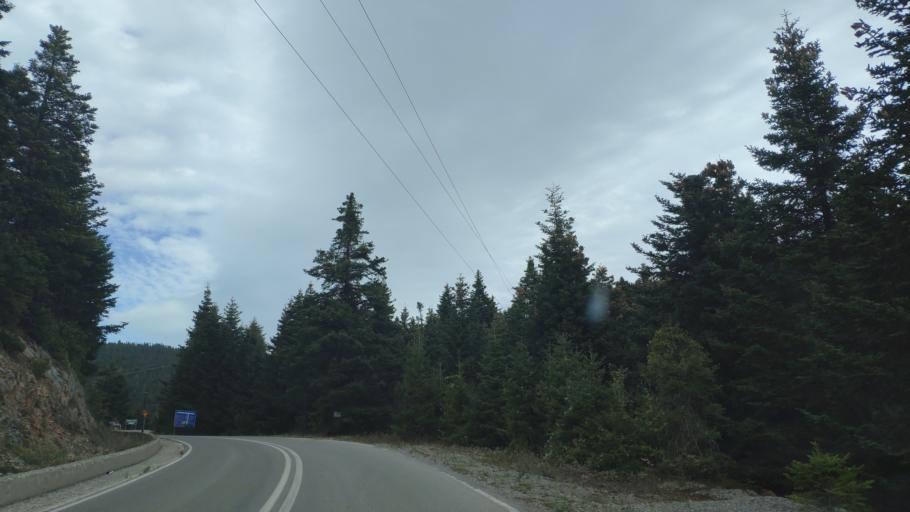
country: GR
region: Central Greece
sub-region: Nomos Fokidos
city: Amfissa
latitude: 38.7029
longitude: 22.3141
